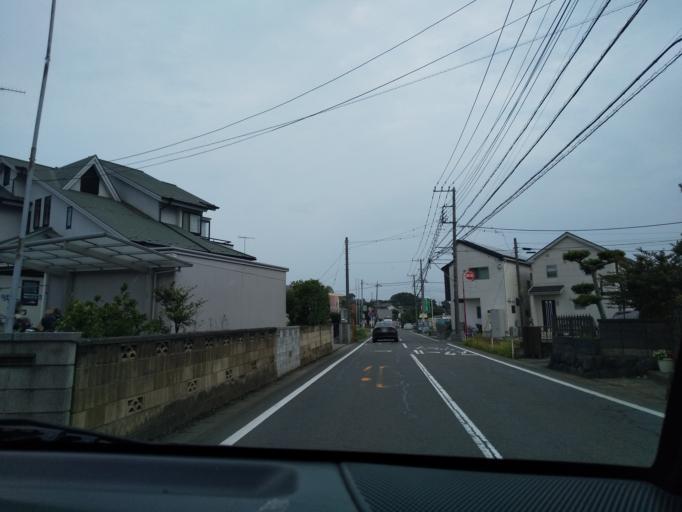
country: JP
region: Kanagawa
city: Atsugi
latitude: 35.3902
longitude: 139.3868
